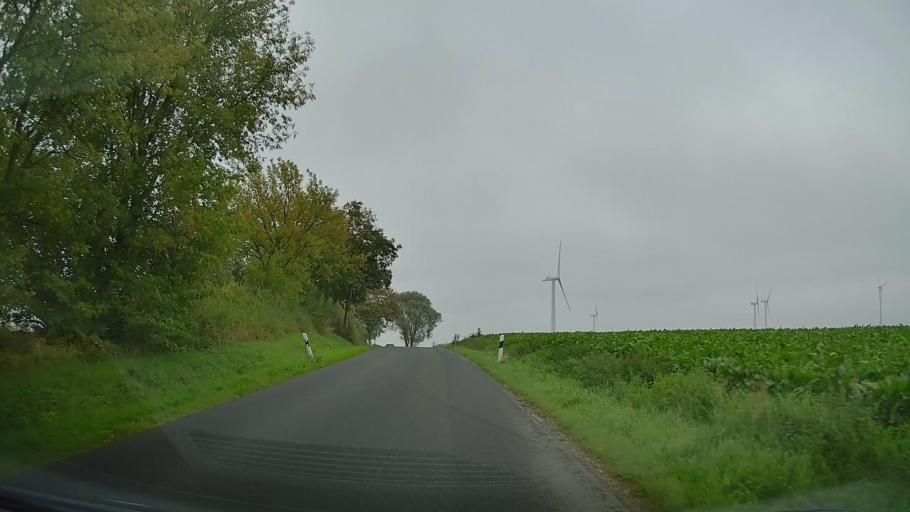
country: DE
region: Mecklenburg-Vorpommern
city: Hornstorf
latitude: 53.9266
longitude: 11.5461
